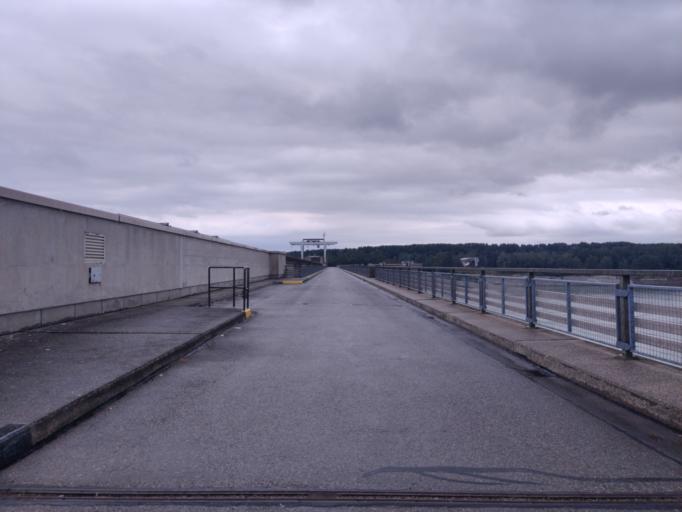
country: AT
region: Lower Austria
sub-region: Politischer Bezirk Korneuburg
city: Spillern
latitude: 48.3525
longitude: 16.2429
